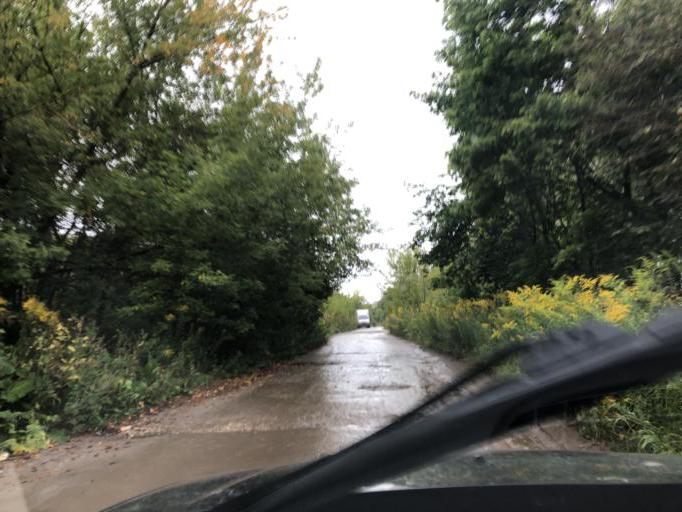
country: RU
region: Tula
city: Mendeleyevskiy
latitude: 54.1697
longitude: 37.5519
